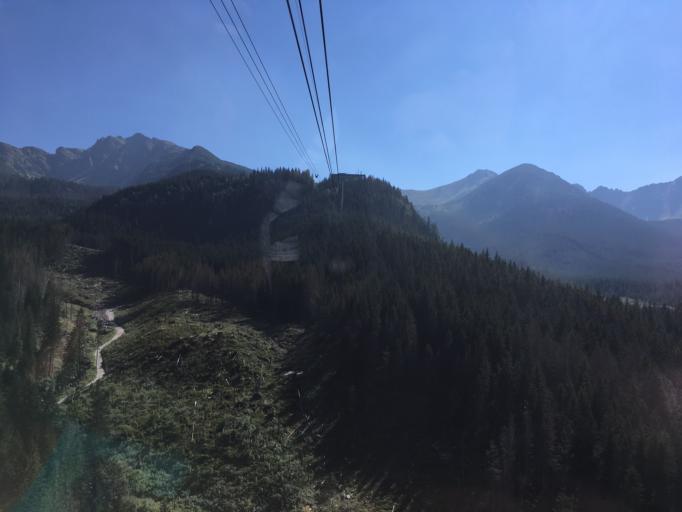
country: PL
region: Lesser Poland Voivodeship
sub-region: Powiat tatrzanski
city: Zakopane
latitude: 49.2585
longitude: 19.9758
